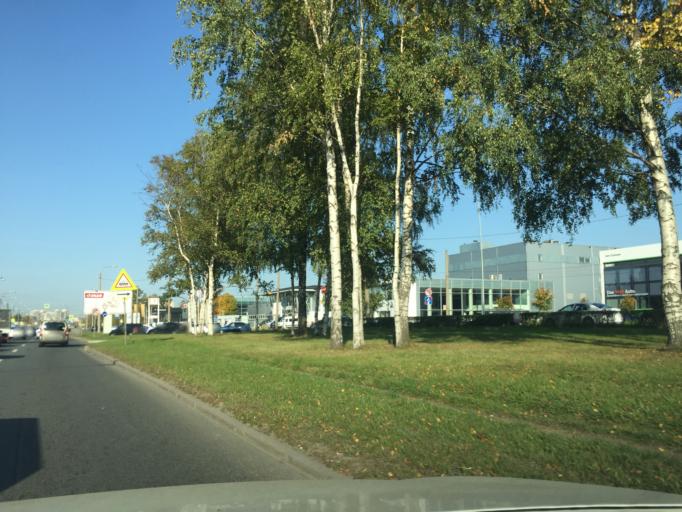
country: RU
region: Leningrad
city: Akademicheskoe
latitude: 60.0056
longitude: 30.4358
